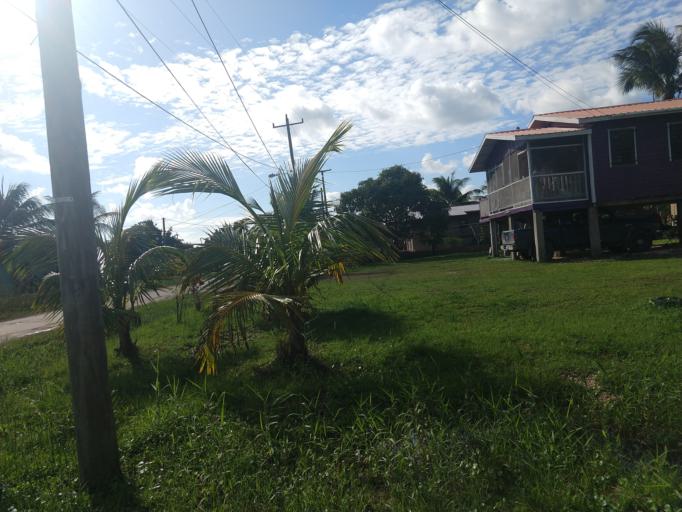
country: BZ
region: Belize
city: Belize City
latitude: 17.5720
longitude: -88.4188
